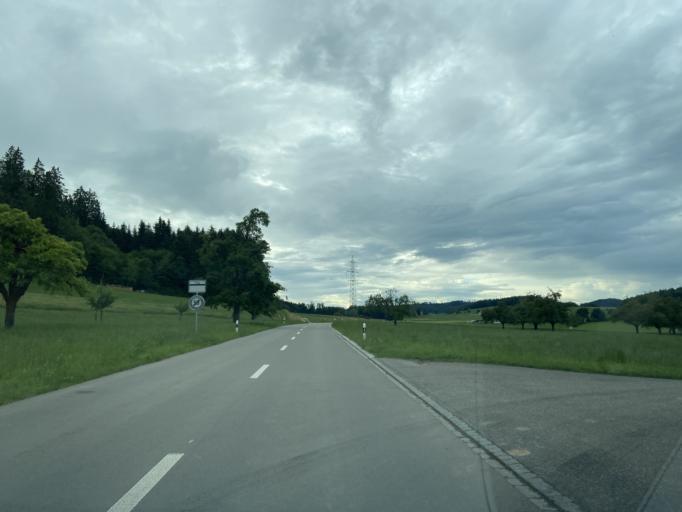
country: CH
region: Thurgau
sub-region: Muenchwilen District
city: Aadorf
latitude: 47.4722
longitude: 8.8869
